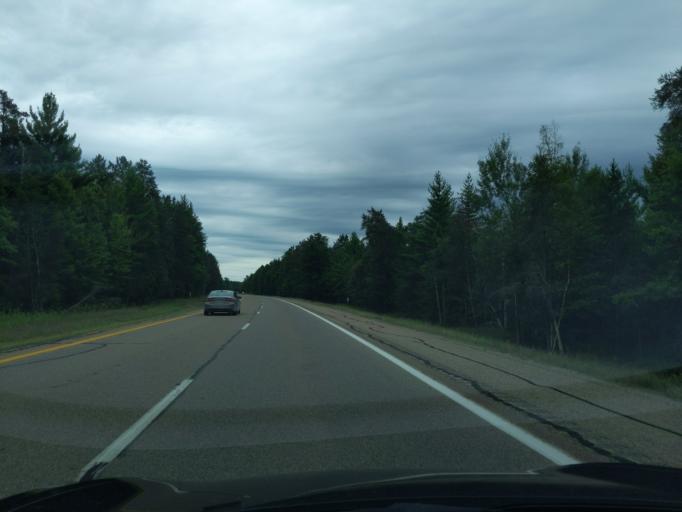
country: US
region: Michigan
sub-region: Roscommon County
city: Houghton Lake
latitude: 44.2351
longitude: -84.8027
